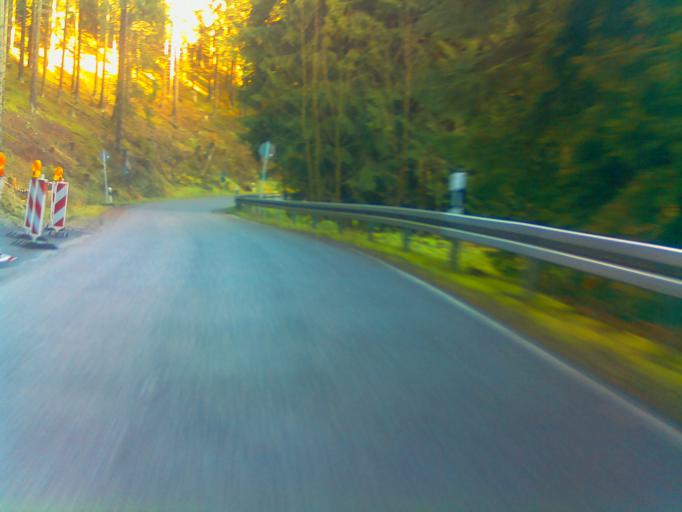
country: DE
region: Thuringia
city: Goldisthal
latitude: 50.5382
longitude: 10.9978
